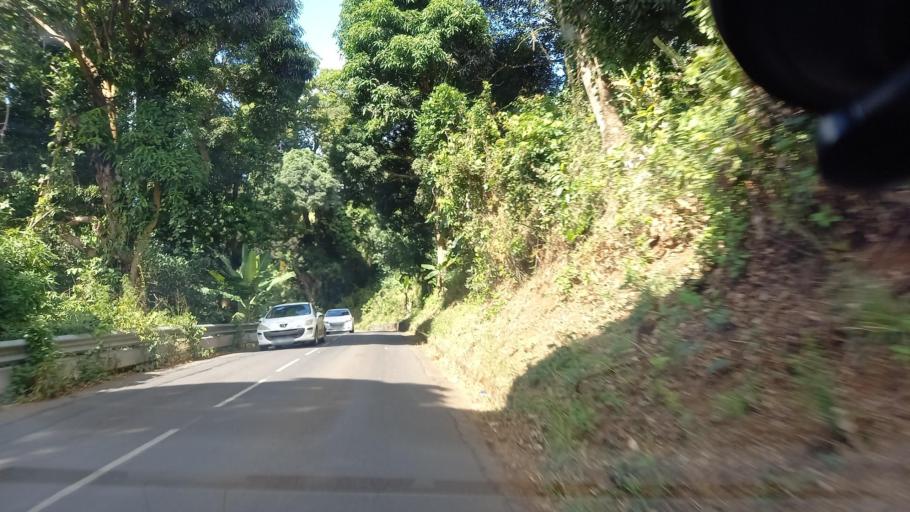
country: YT
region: Mamoudzou
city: Mamoudzou
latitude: -12.7926
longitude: 45.1918
